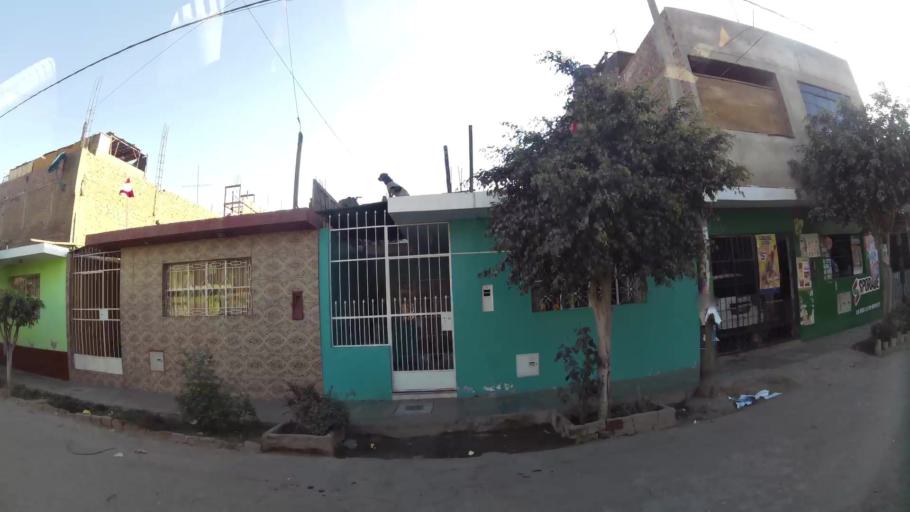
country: PE
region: Ica
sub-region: Provincia de Ica
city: Ica
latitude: -14.0693
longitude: -75.7192
